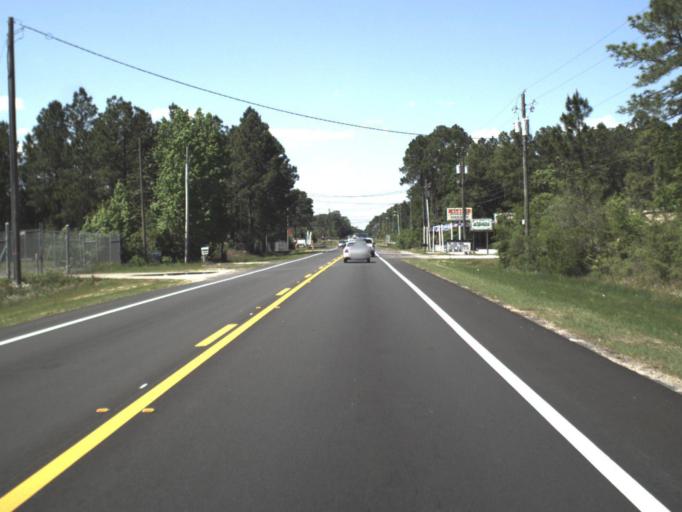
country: US
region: Florida
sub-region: Bay County
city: Hiland Park
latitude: 30.1887
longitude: -85.6078
